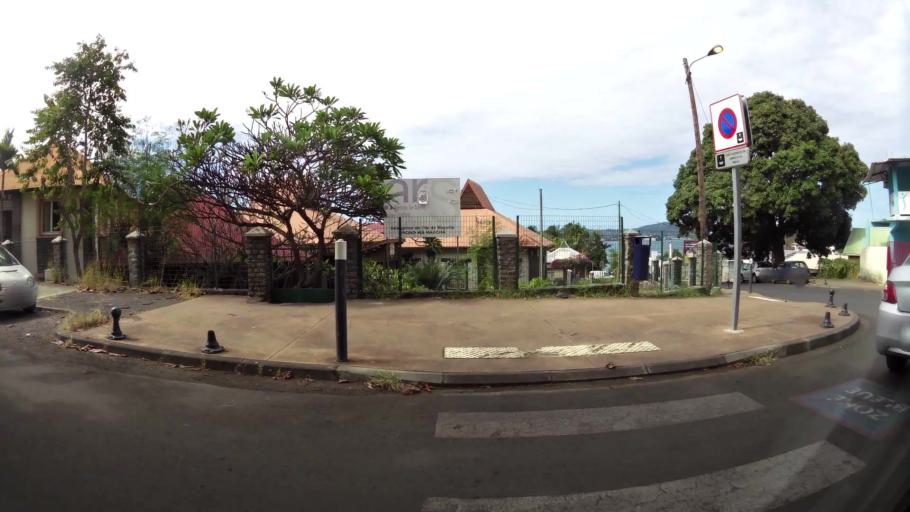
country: YT
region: Mamoudzou
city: Mamoudzou
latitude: -12.7777
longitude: 45.2286
